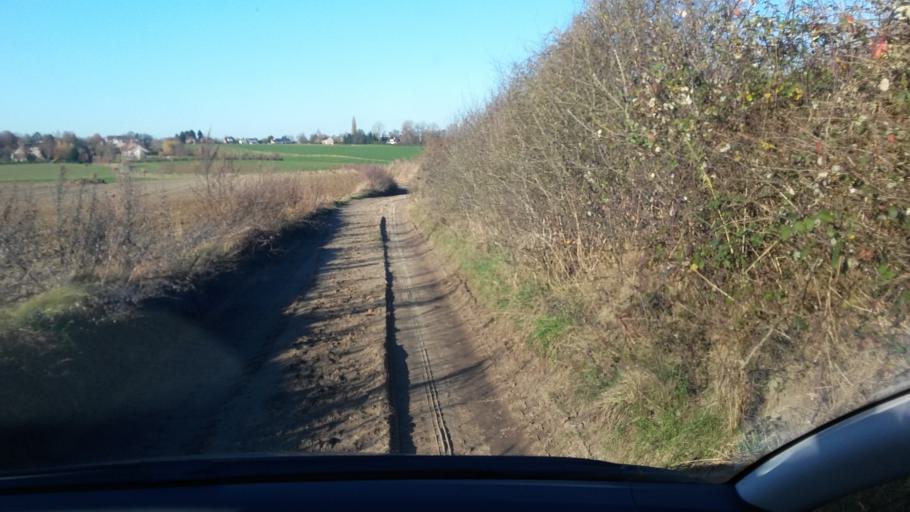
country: BE
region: Wallonia
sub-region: Province du Brabant Wallon
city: Waterloo
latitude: 50.6879
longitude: 4.4268
